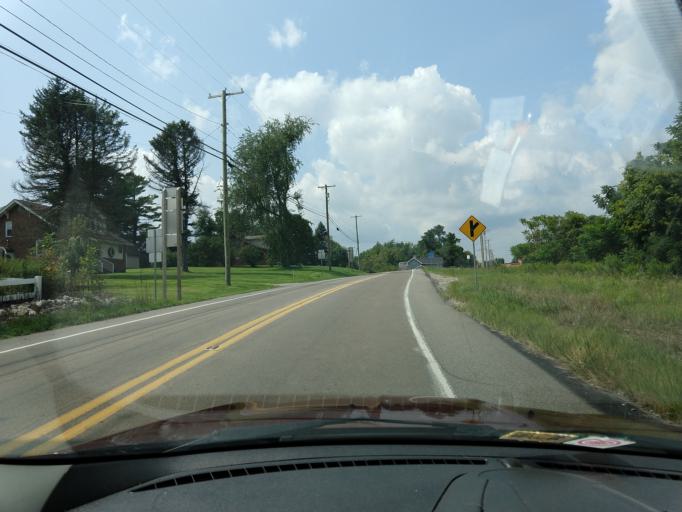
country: US
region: Pennsylvania
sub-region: Washington County
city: Baidland
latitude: 40.1953
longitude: -79.9988
